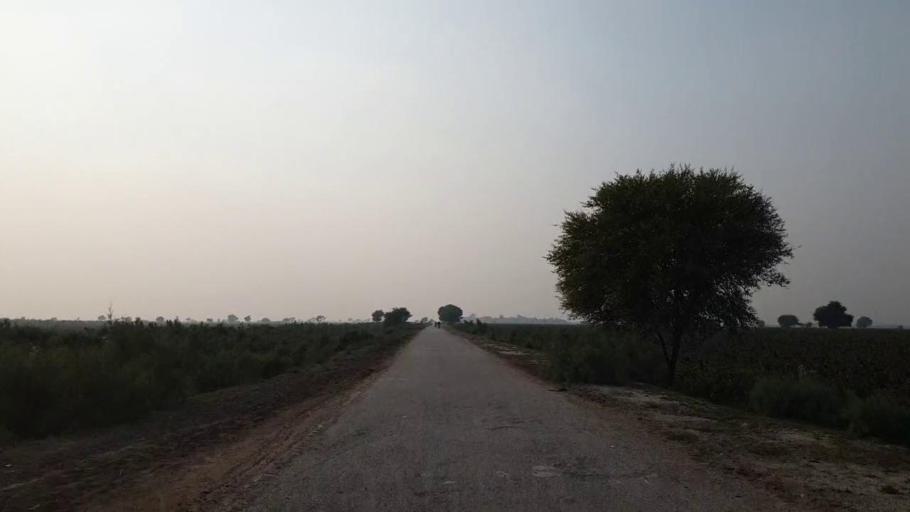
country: PK
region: Sindh
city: Bhan
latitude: 26.4885
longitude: 67.7188
